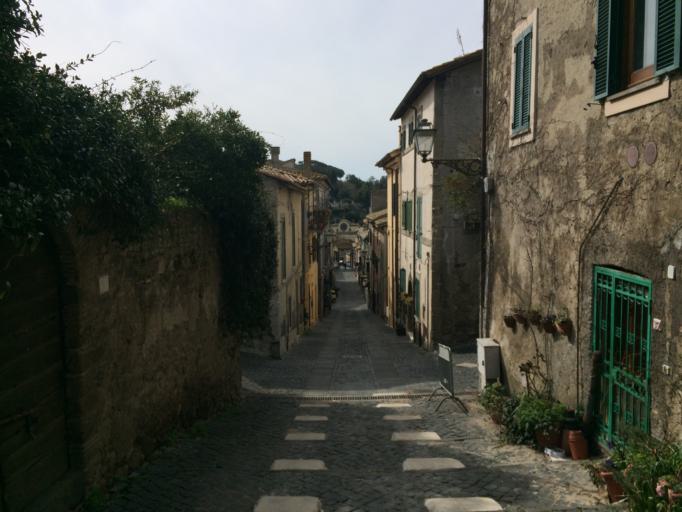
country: IT
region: Latium
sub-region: Citta metropolitana di Roma Capitale
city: Anguillara Sabazia
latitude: 42.0940
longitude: 12.2700
